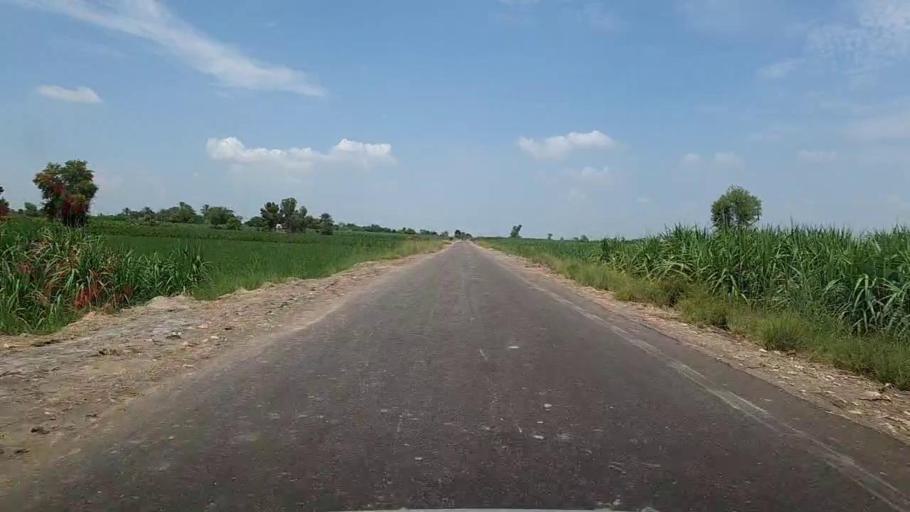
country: PK
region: Sindh
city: Bhiria
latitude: 26.9344
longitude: 68.2162
